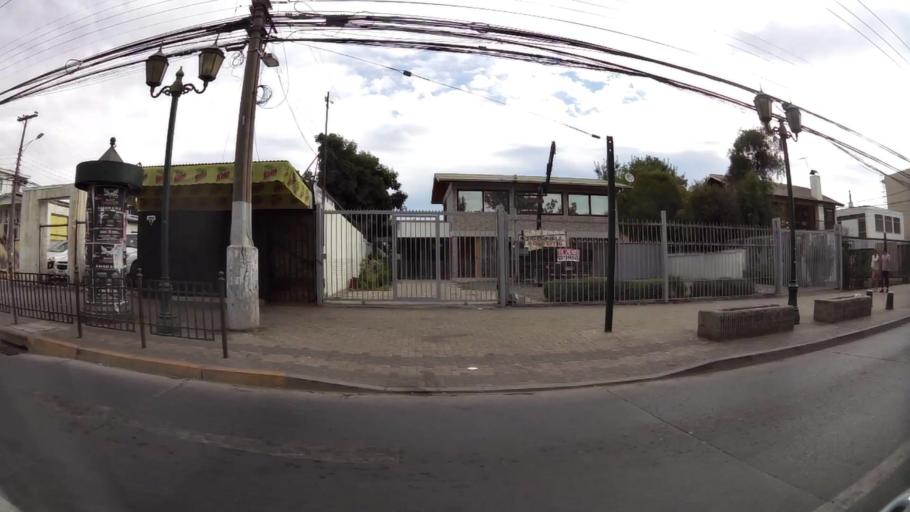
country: CL
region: O'Higgins
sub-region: Provincia de Cachapoal
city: Rancagua
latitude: -34.1658
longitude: -70.7400
